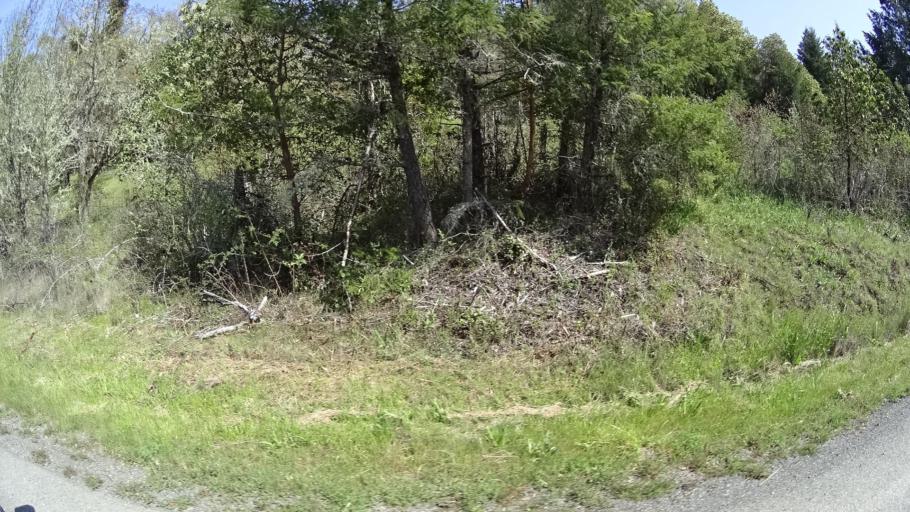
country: US
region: California
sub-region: Humboldt County
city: Redway
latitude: 40.3023
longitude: -123.6541
